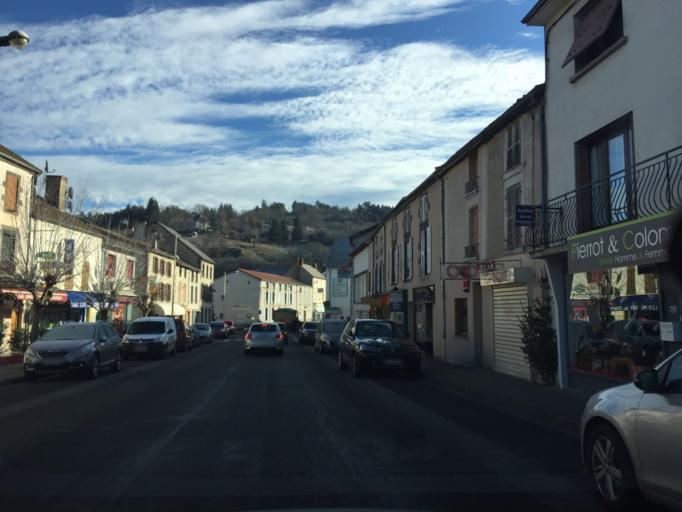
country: FR
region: Auvergne
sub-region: Departement du Puy-de-Dome
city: Gelles
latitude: 45.8685
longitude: 2.6740
